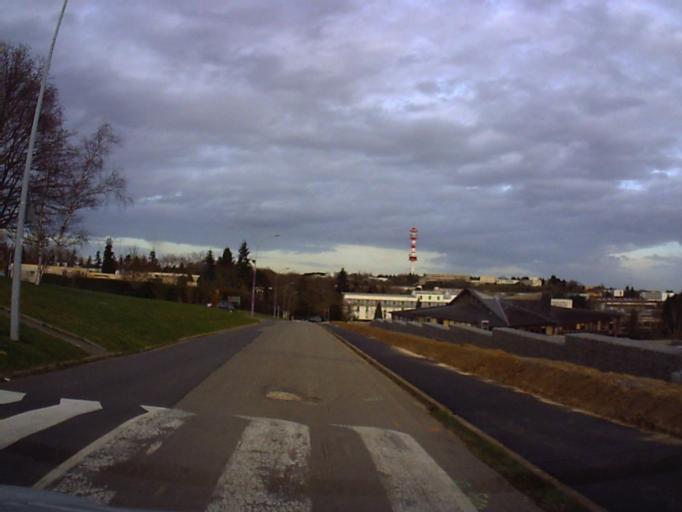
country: FR
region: Brittany
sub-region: Departement d'Ille-et-Vilaine
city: Rennes
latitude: 48.1226
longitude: -1.6424
